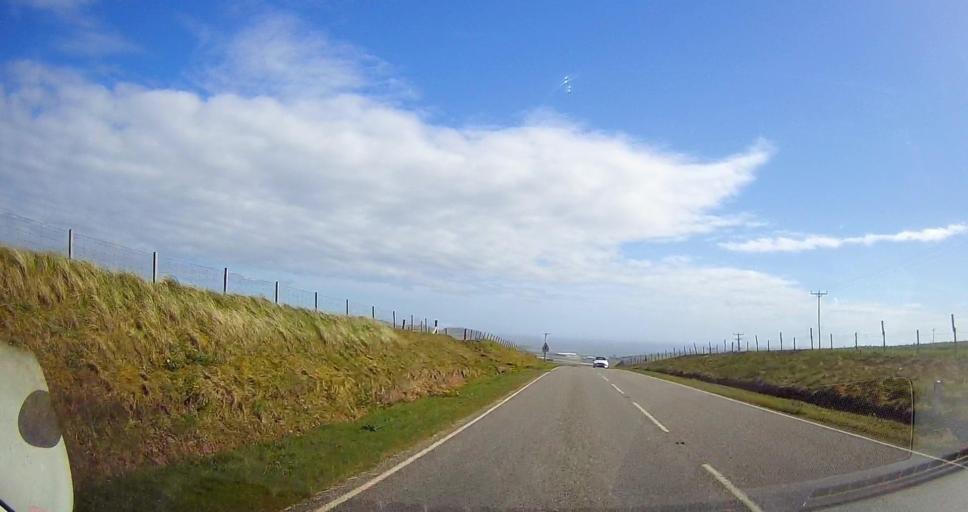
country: GB
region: Scotland
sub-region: Shetland Islands
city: Sandwick
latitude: 59.8970
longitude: -1.3034
